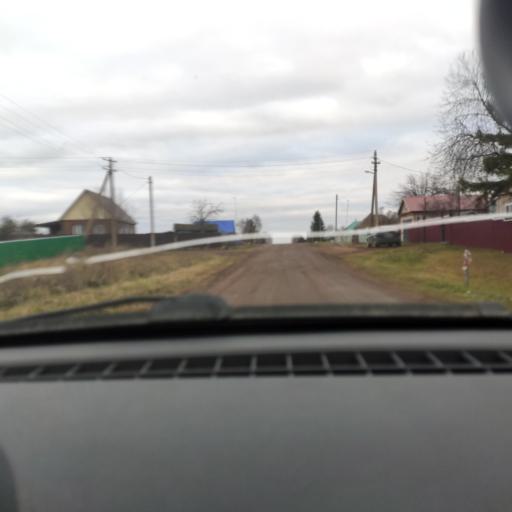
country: RU
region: Bashkortostan
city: Ulukulevo
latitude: 54.4397
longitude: 56.4586
